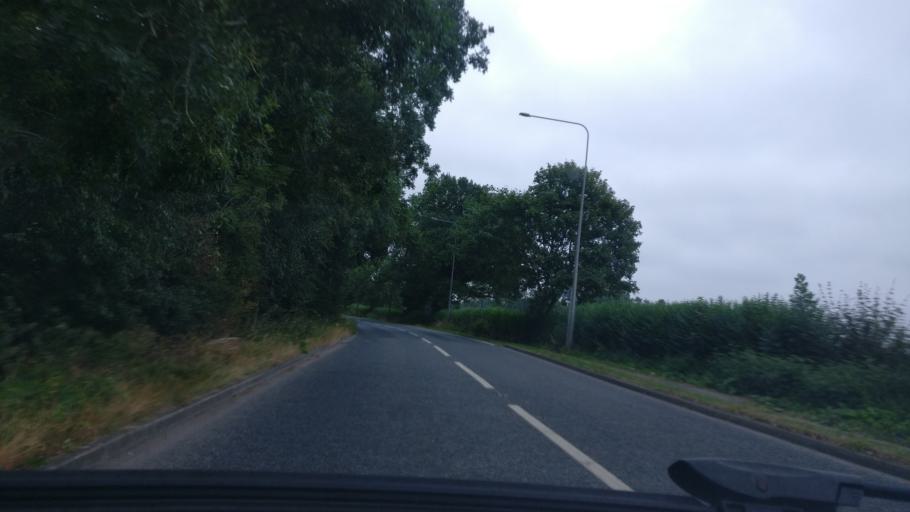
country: GB
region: England
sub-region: East Riding of Yorkshire
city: Leven
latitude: 53.8806
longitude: -0.3119
